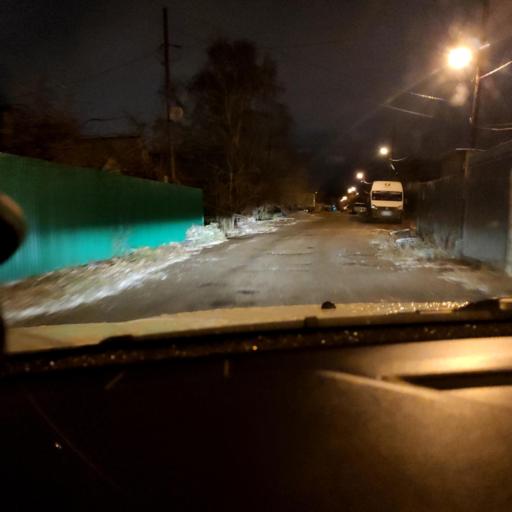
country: RU
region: Samara
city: Samara
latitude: 53.1827
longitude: 50.2315
